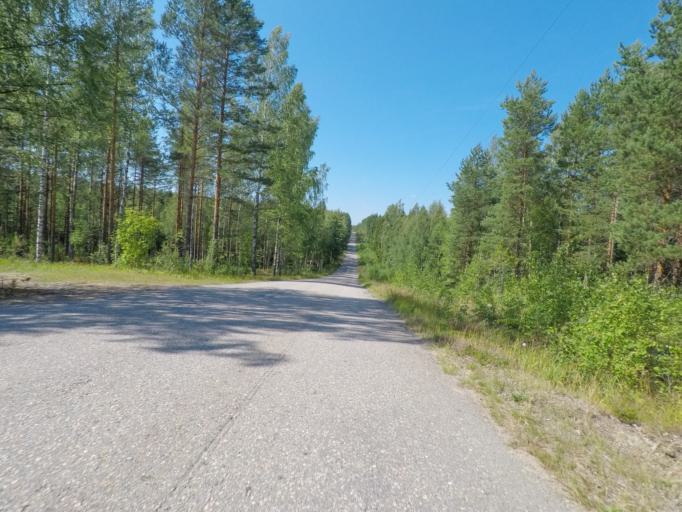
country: FI
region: Southern Savonia
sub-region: Mikkeli
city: Puumala
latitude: 61.4224
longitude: 28.1401
